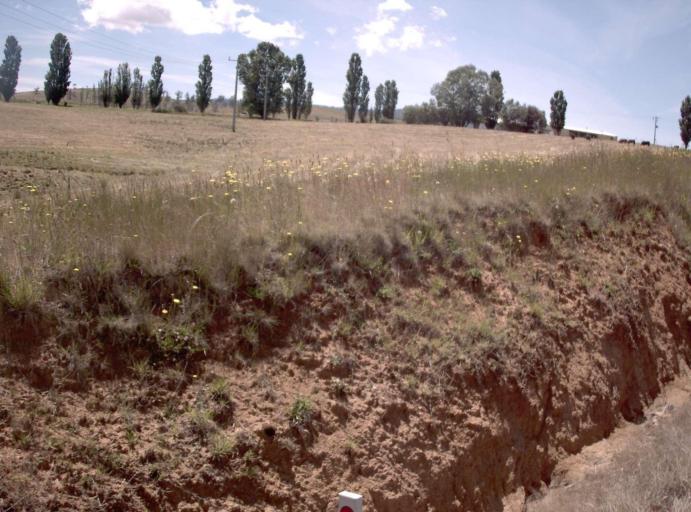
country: AU
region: Victoria
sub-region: Alpine
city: Mount Beauty
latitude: -37.1074
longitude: 147.6040
